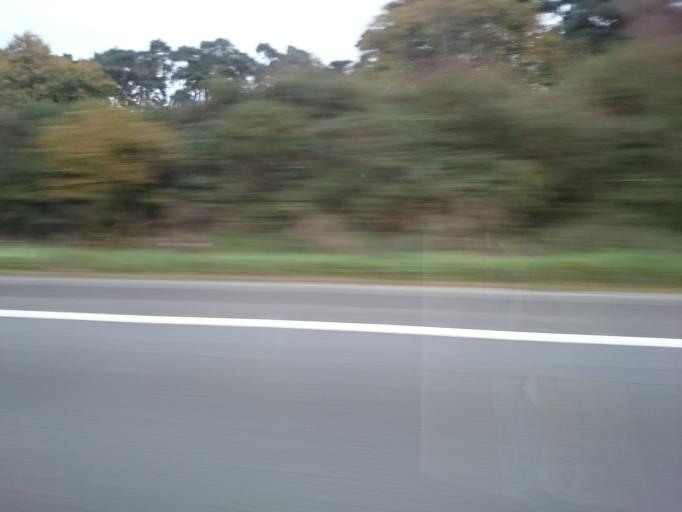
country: FR
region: Pays de la Loire
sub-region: Departement de la Loire-Atlantique
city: Orvault
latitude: 47.2914
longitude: -1.6113
